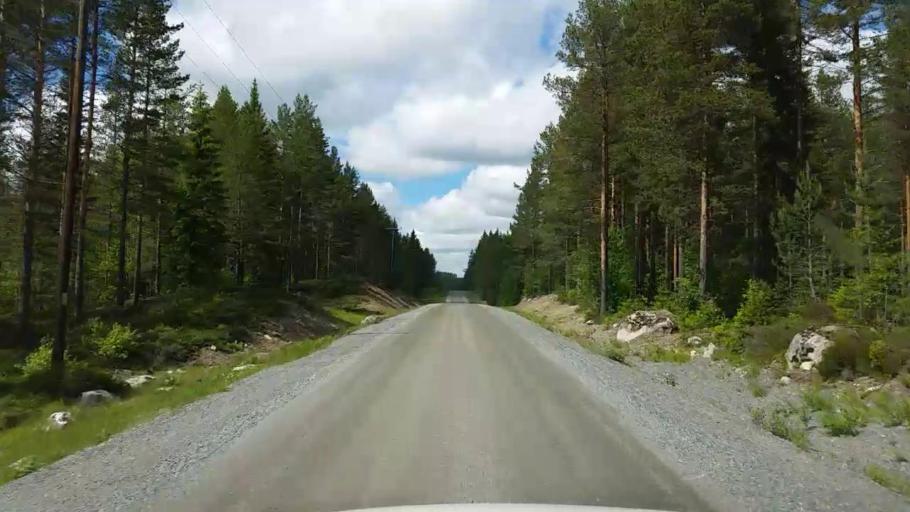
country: SE
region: Gaevleborg
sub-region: Bollnas Kommun
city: Vittsjo
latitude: 61.0746
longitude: 16.2710
